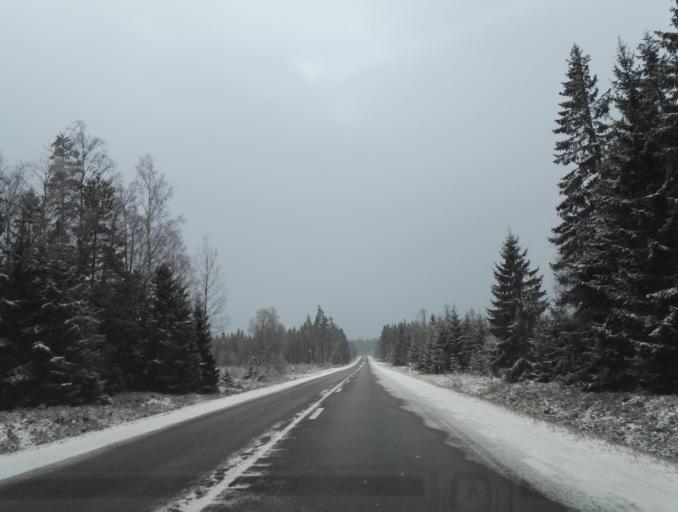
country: SE
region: Kronoberg
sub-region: Uppvidinge Kommun
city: Lenhovda
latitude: 56.9079
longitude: 15.3676
